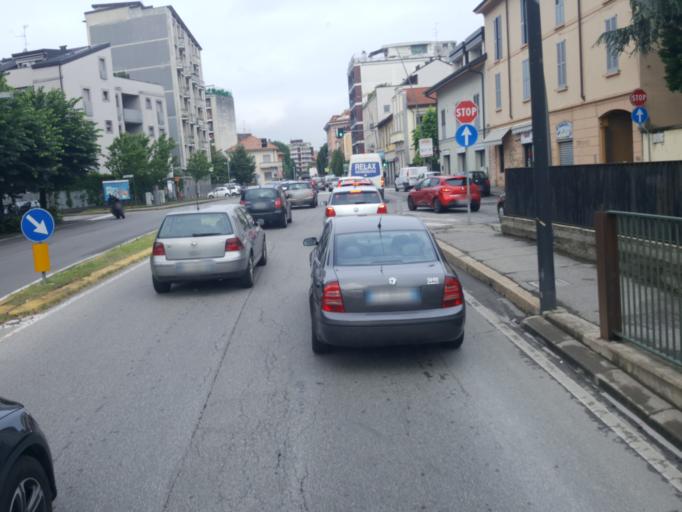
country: IT
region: Lombardy
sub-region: Provincia di Monza e Brianza
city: Monza
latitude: 45.5887
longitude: 9.2909
